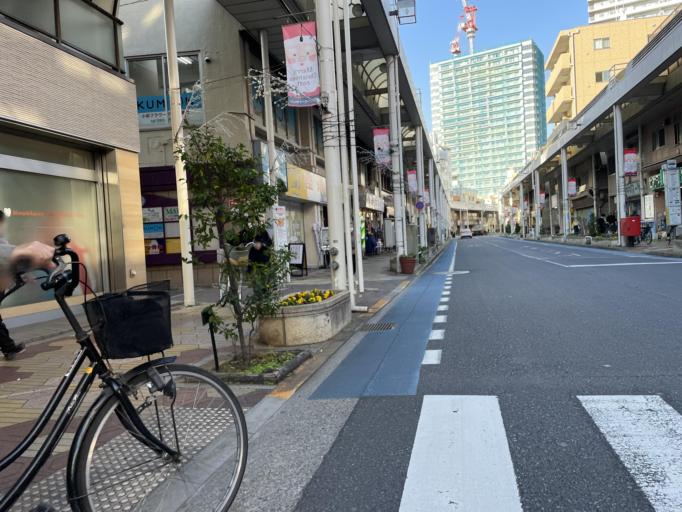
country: JP
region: Chiba
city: Matsudo
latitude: 35.7297
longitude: 139.8816
